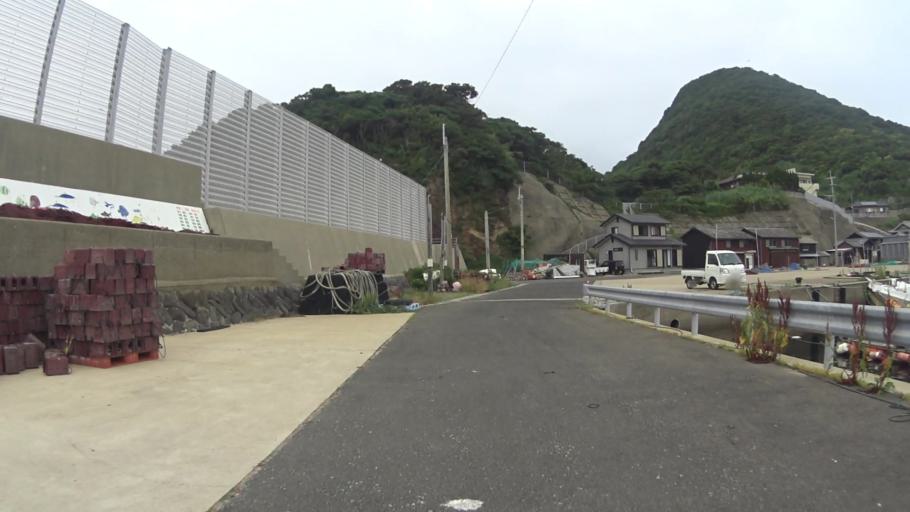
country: JP
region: Nagasaki
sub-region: Hirado Shi
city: Hirado
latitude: 33.1937
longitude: 129.3552
